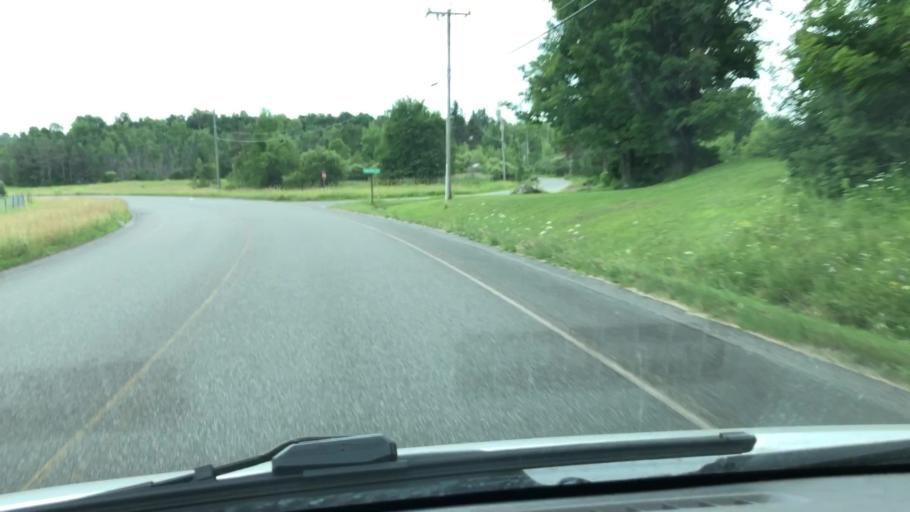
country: US
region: Massachusetts
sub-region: Berkshire County
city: Adams
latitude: 42.5348
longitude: -73.0573
